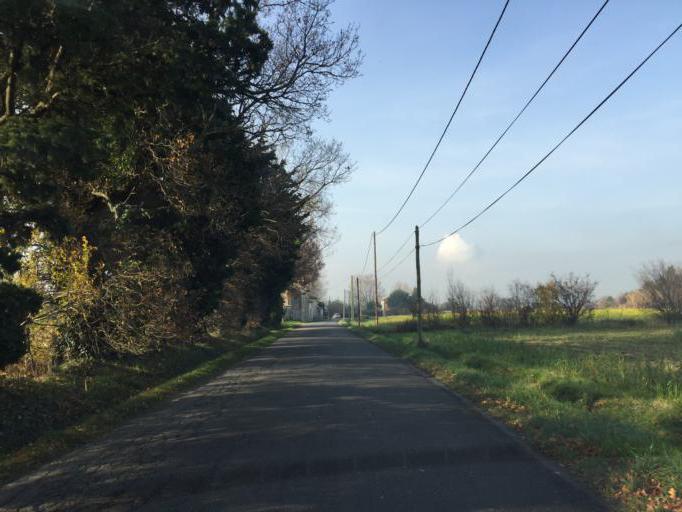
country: FR
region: Provence-Alpes-Cote d'Azur
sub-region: Departement du Vaucluse
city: Jonquieres
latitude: 44.1265
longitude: 4.8871
